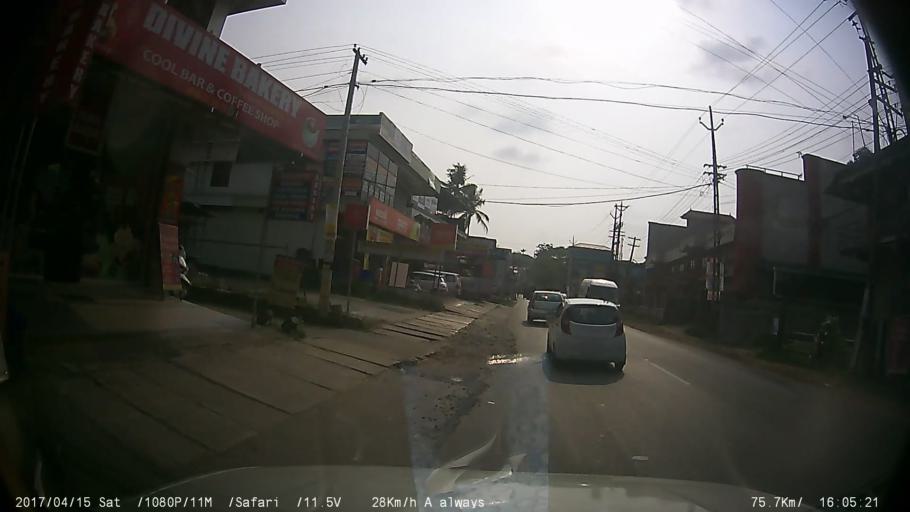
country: IN
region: Kerala
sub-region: Kottayam
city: Kottayam
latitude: 9.6712
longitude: 76.5618
